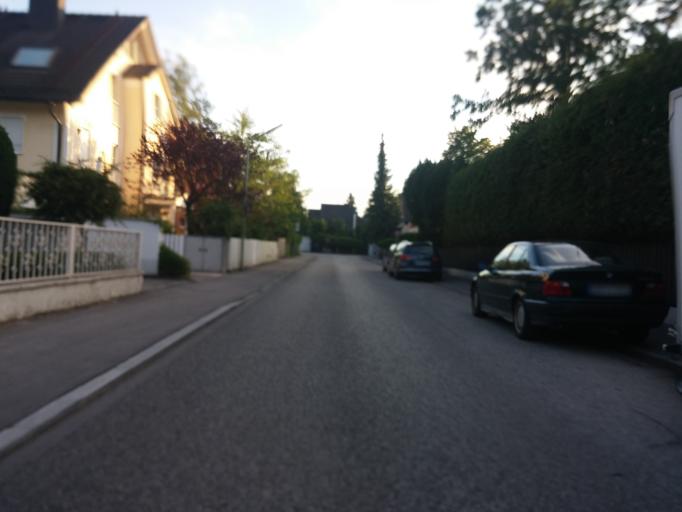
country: DE
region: Bavaria
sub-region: Upper Bavaria
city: Haar
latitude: 48.1068
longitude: 11.6981
